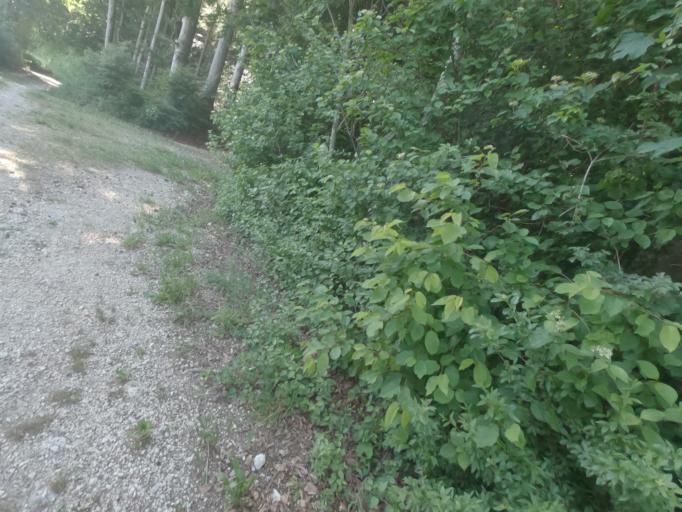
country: CH
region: Solothurn
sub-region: Bezirk Lebern
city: Langendorf
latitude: 47.2419
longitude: 7.5294
